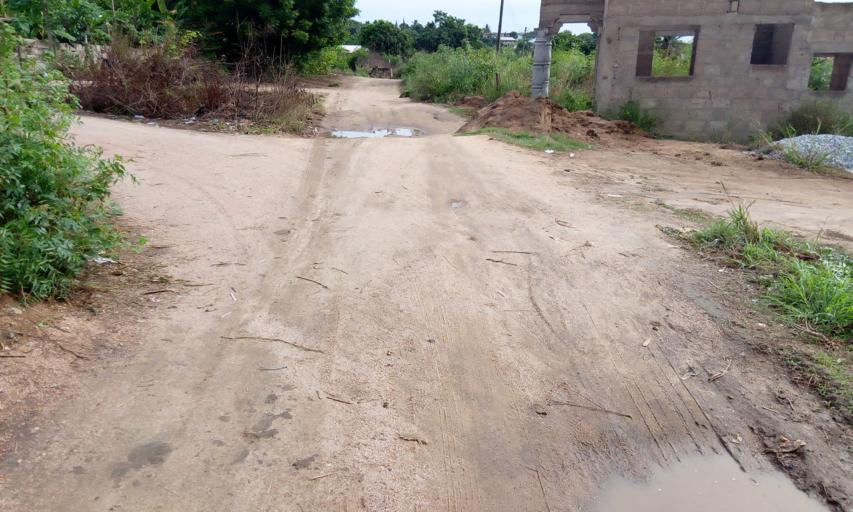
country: GH
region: Central
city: Winneba
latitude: 5.3597
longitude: -0.6196
